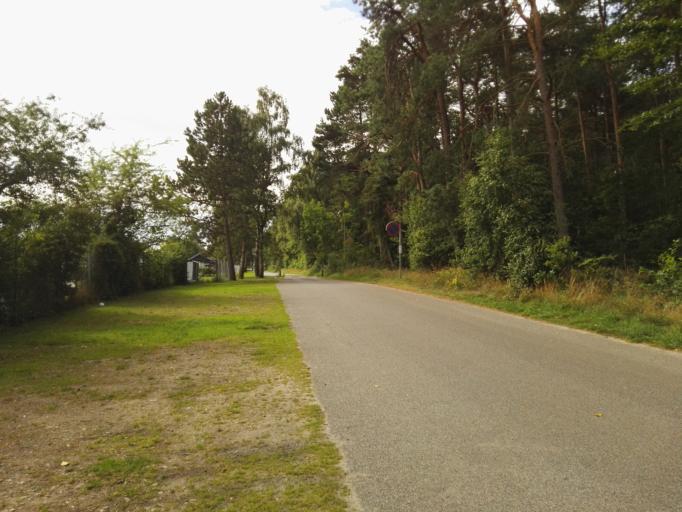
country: DK
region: Zealand
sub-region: Odsherred Kommune
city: Nykobing Sjaelland
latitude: 55.9409
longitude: 11.6833
